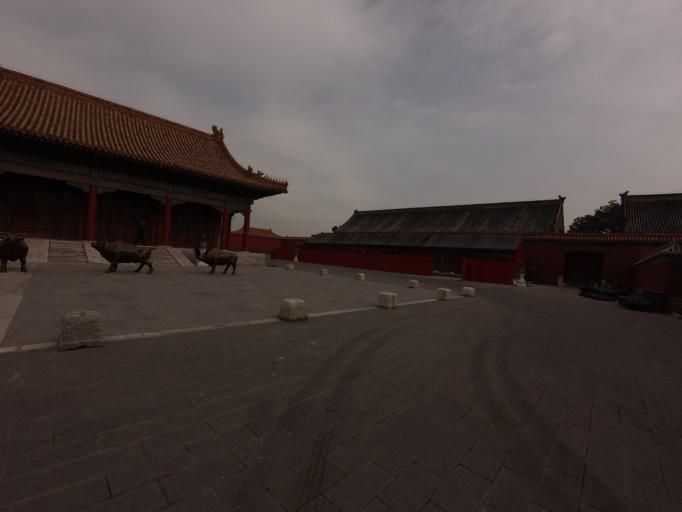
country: CN
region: Beijing
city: Beijing
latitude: 39.9164
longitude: 116.3926
